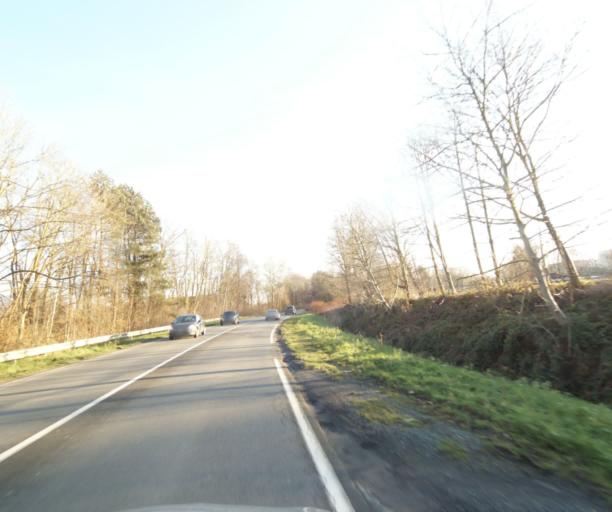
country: FR
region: Nord-Pas-de-Calais
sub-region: Departement du Nord
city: Famars
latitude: 50.3282
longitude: 3.5170
